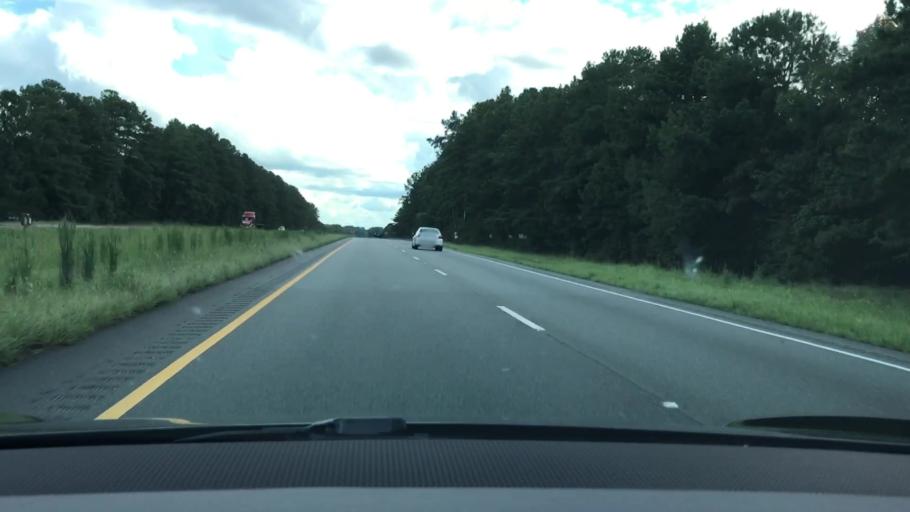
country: US
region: Alabama
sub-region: Pike County
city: Troy
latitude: 31.9660
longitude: -86.0263
